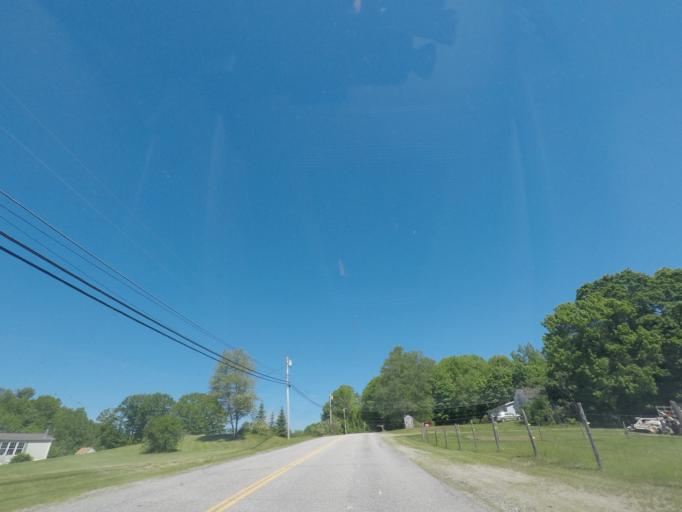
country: US
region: Maine
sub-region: Kennebec County
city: Manchester
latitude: 44.2478
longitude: -69.8984
